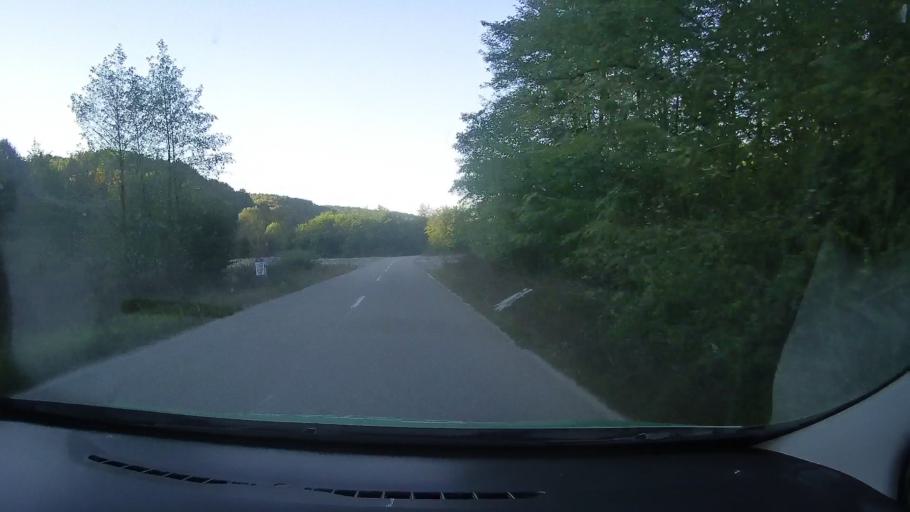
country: RO
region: Timis
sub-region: Comuna Fardea
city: Fardea
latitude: 45.6941
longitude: 22.1602
